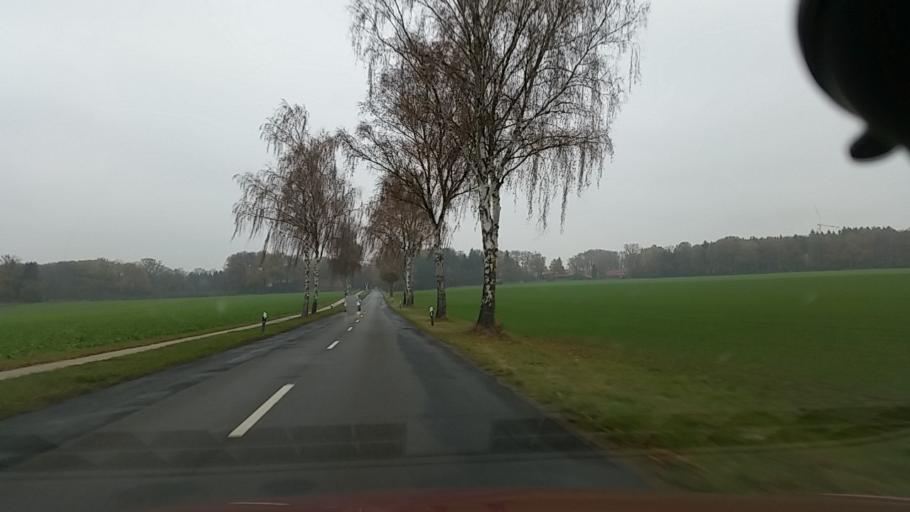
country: DE
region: Lower Saxony
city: Wrestedt
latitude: 52.9330
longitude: 10.5730
